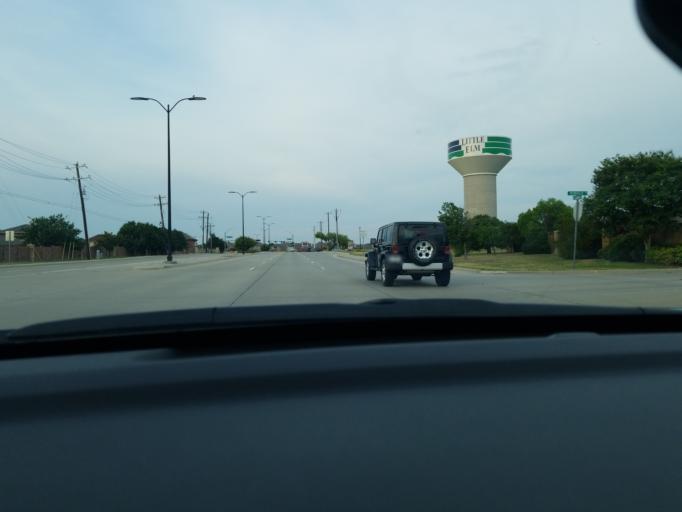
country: US
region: Texas
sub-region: Denton County
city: Little Elm
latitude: 33.1690
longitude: -96.8999
